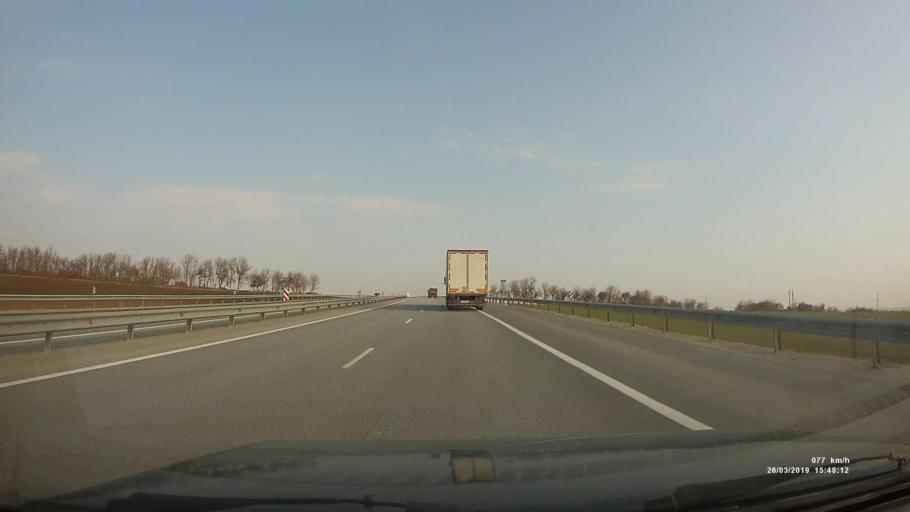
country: RU
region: Rostov
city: Chaltyr
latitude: 47.2801
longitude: 39.4479
